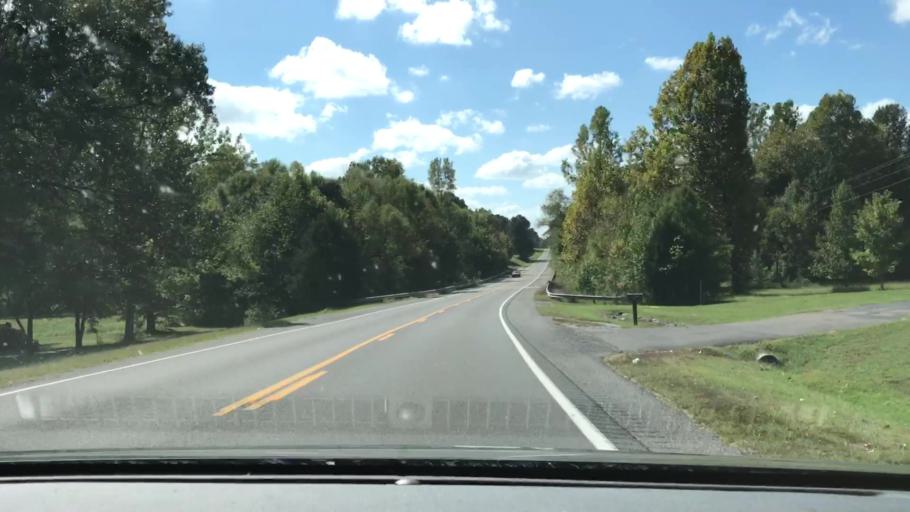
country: US
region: Kentucky
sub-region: McCracken County
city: Reidland
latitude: 36.9118
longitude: -88.5216
